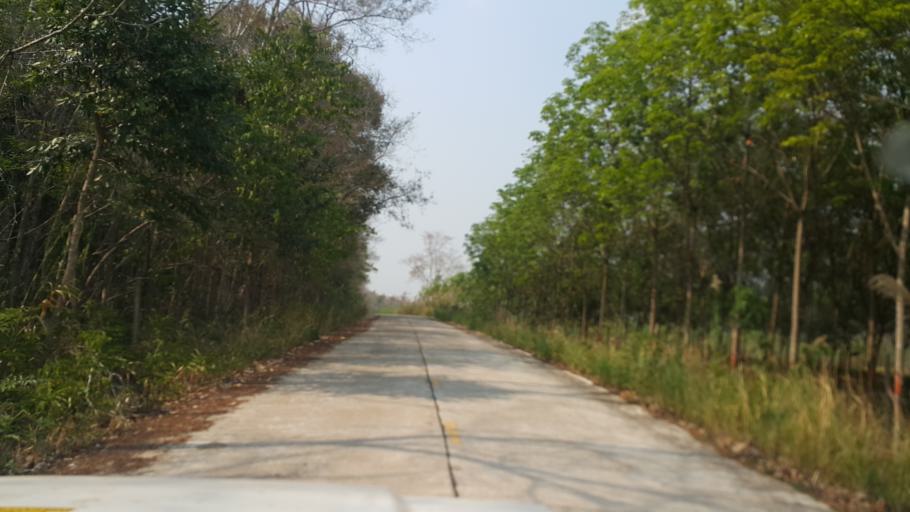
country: TH
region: Nakhon Phanom
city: Ban Phaeng
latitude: 17.9748
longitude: 104.1504
